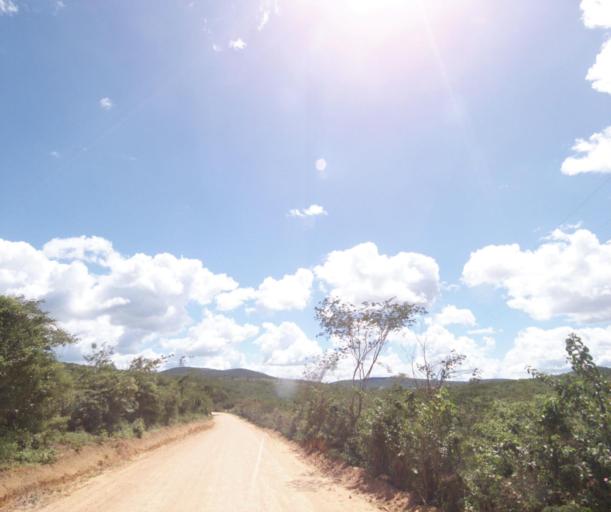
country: BR
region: Bahia
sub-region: Pocoes
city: Pocoes
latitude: -14.2975
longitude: -40.6394
